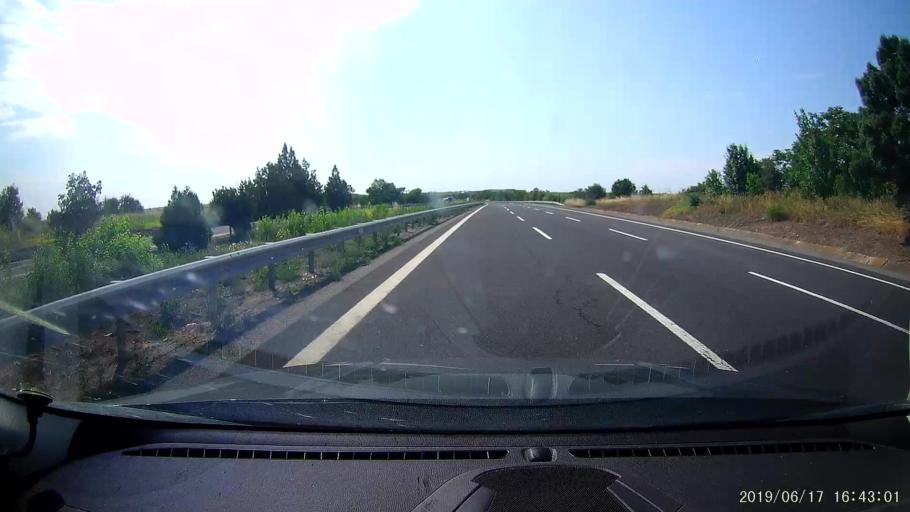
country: TR
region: Kirklareli
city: Luleburgaz
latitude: 41.4776
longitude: 27.3063
